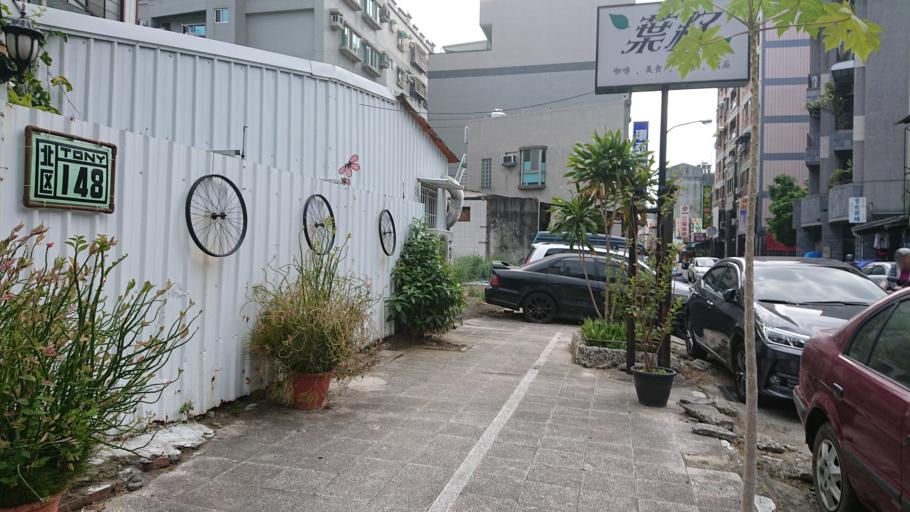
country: TW
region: Taiwan
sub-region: Tainan
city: Tainan
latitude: 23.0032
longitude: 120.2048
